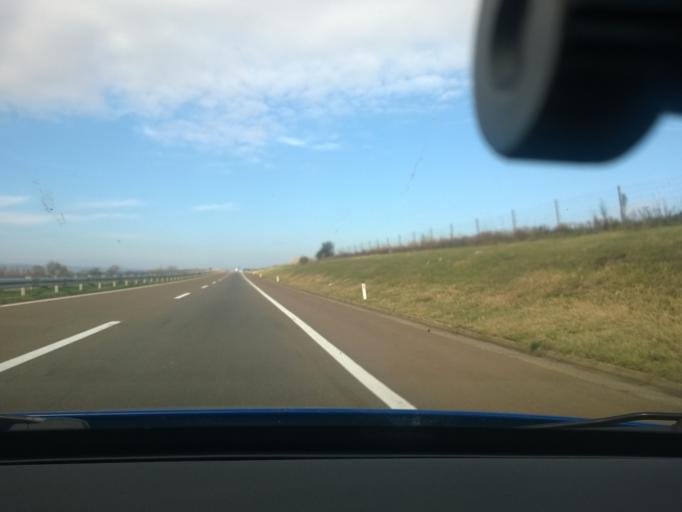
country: RS
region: Central Serbia
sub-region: Nisavski Okrug
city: Aleksinac
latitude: 43.5807
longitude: 21.6611
